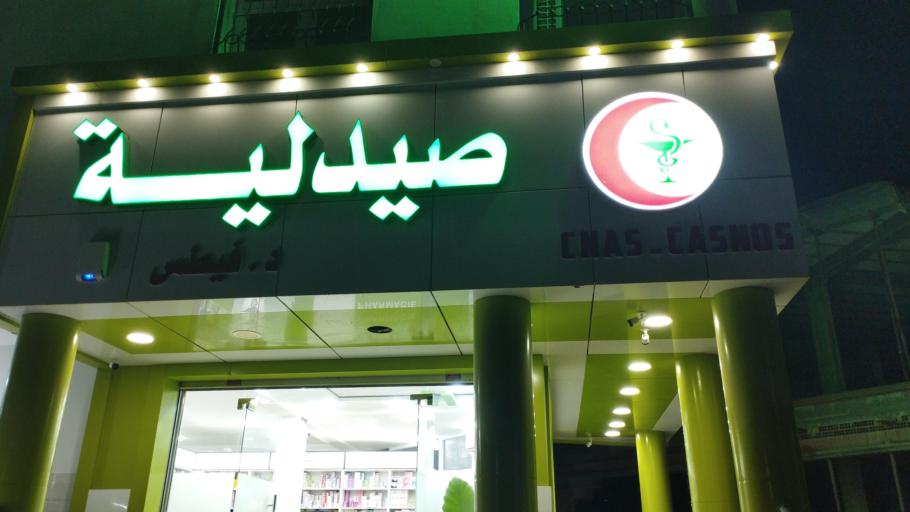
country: DZ
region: Djelfa
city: Birine
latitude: 35.6301
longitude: 3.2260
